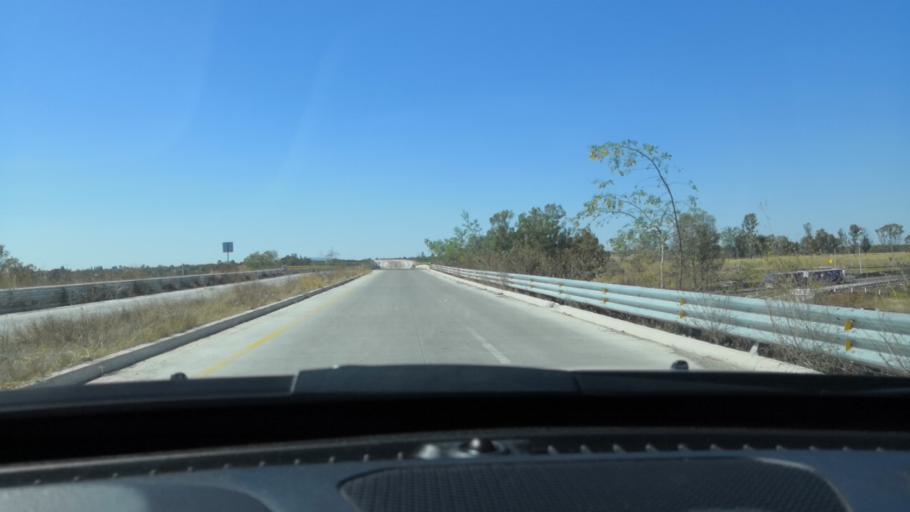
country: MX
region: Guanajuato
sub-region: Leon
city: Centro Familiar la Soledad
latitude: 21.0997
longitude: -101.7783
